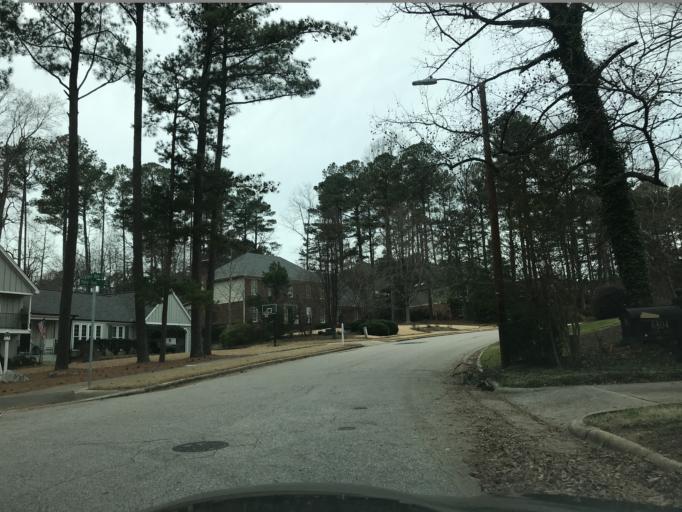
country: US
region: North Carolina
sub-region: Wake County
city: West Raleigh
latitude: 35.8730
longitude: -78.6076
